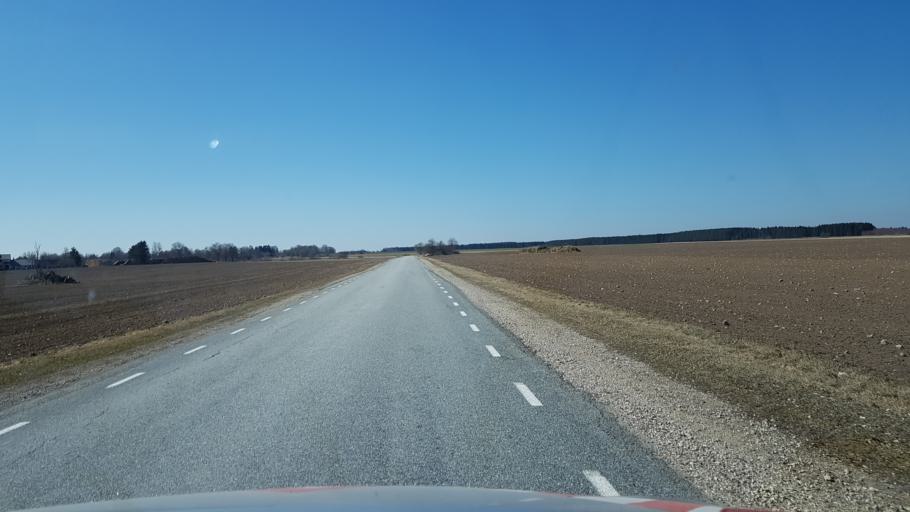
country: EE
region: Laeaene-Virumaa
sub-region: Rakke vald
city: Rakke
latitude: 59.0435
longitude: 26.3633
